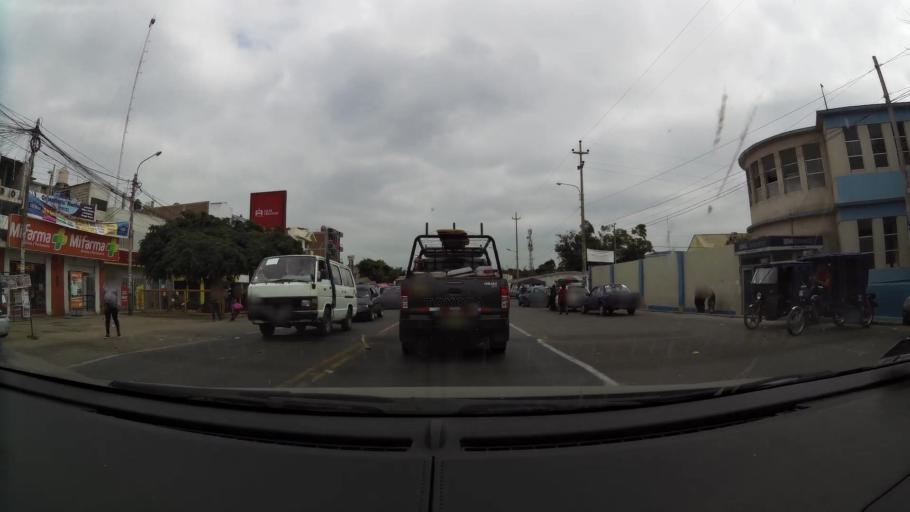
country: PE
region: La Libertad
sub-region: Ascope
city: Chocope
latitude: -7.7932
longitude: -79.2224
